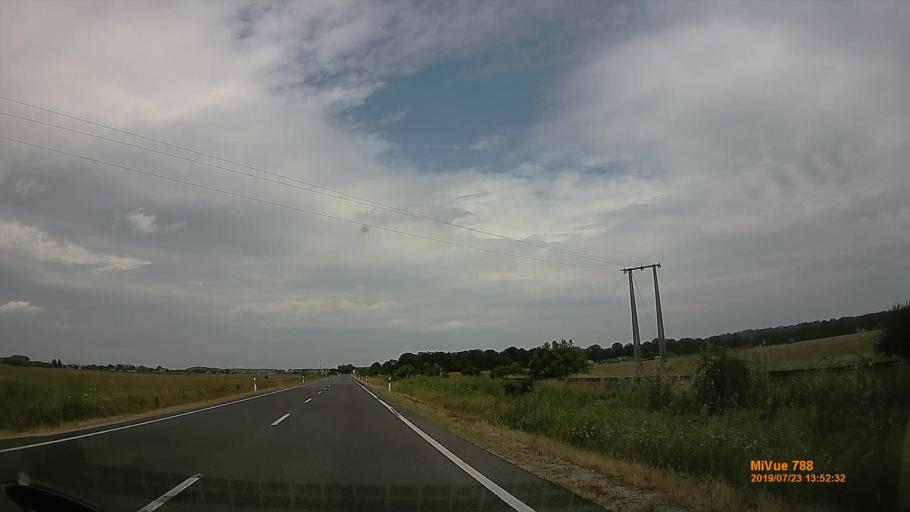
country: HU
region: Hajdu-Bihar
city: Polgar
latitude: 47.9033
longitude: 21.1618
